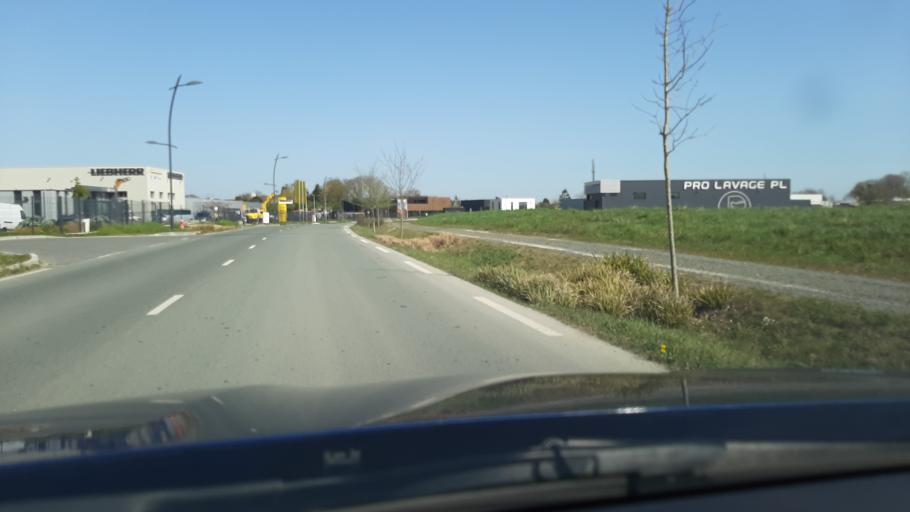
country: FR
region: Pays de la Loire
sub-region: Departement de Maine-et-Loire
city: Pellouailles-les-Vignes
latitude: 47.5178
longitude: -0.4424
